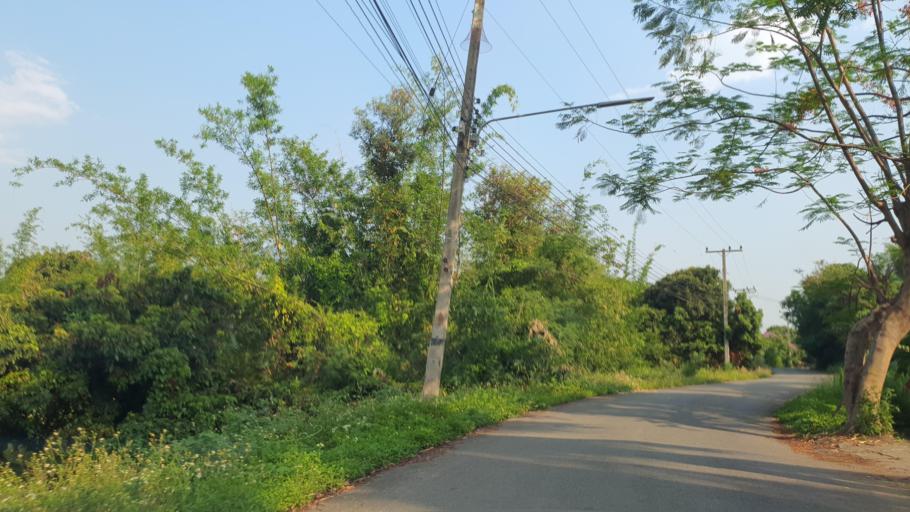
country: TH
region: Chiang Mai
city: Mae Wang
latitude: 18.6763
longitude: 98.8116
